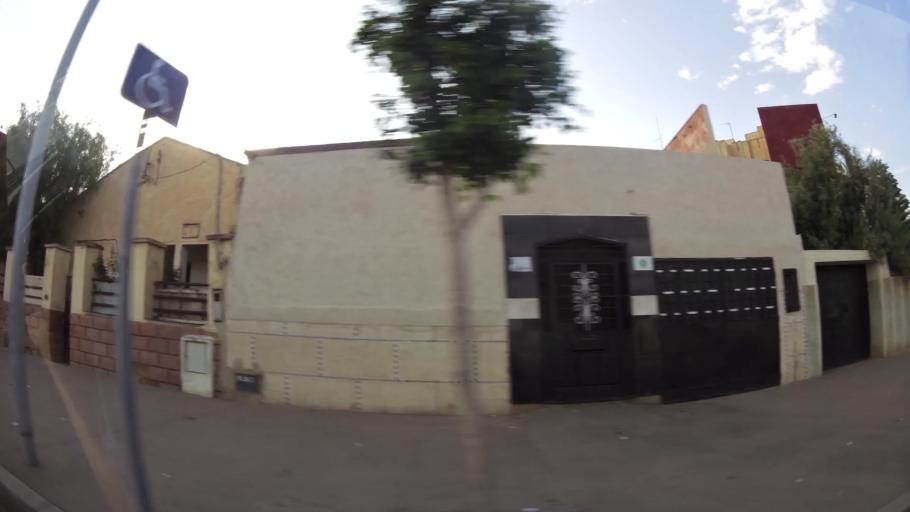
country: MA
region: Oriental
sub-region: Oujda-Angad
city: Oujda
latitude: 34.6764
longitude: -1.9249
